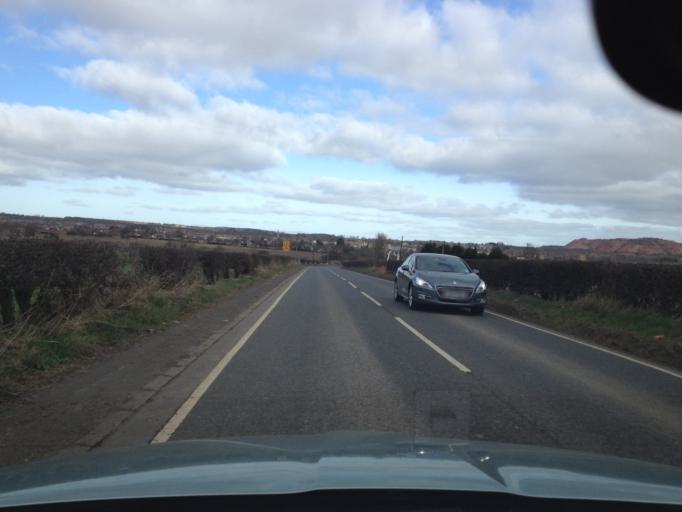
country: GB
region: Scotland
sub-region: West Lothian
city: Broxburn
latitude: 55.9239
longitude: -3.4670
